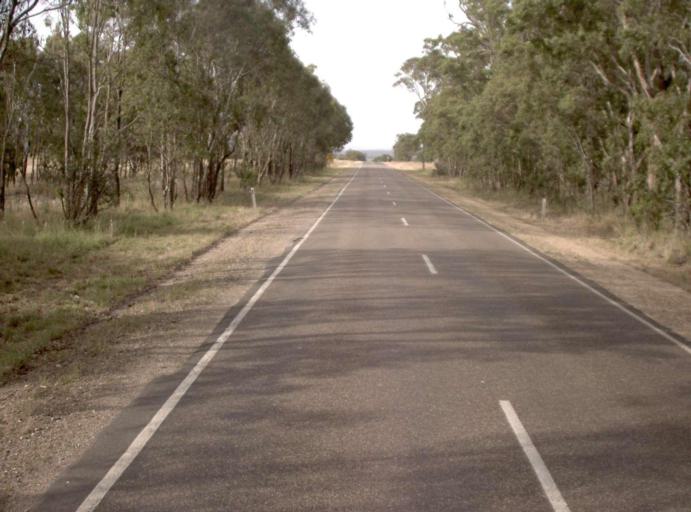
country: AU
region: Victoria
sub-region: Wellington
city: Heyfield
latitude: -38.0287
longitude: 146.6683
